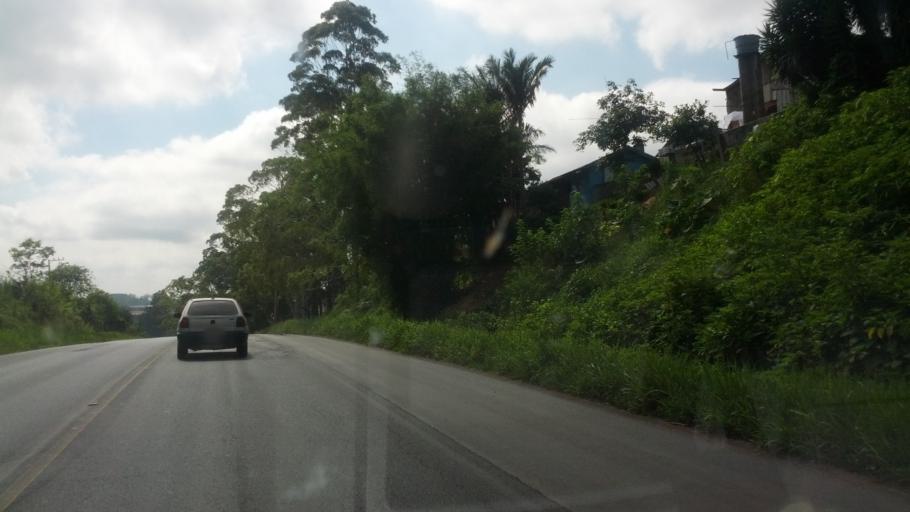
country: BR
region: Santa Catarina
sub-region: Rio Do Sul
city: Rio do Sul
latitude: -27.2594
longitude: -49.9234
